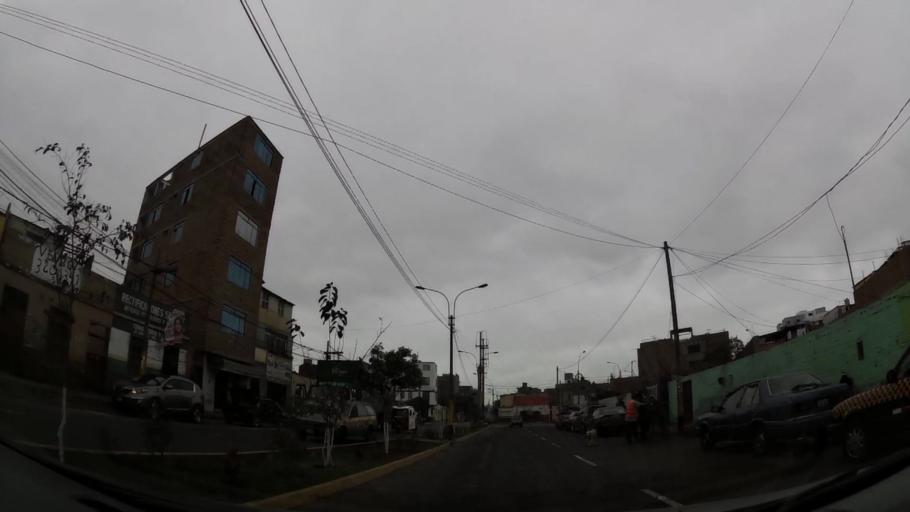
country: PE
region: Lima
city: Lima
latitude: -12.0579
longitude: -77.0520
